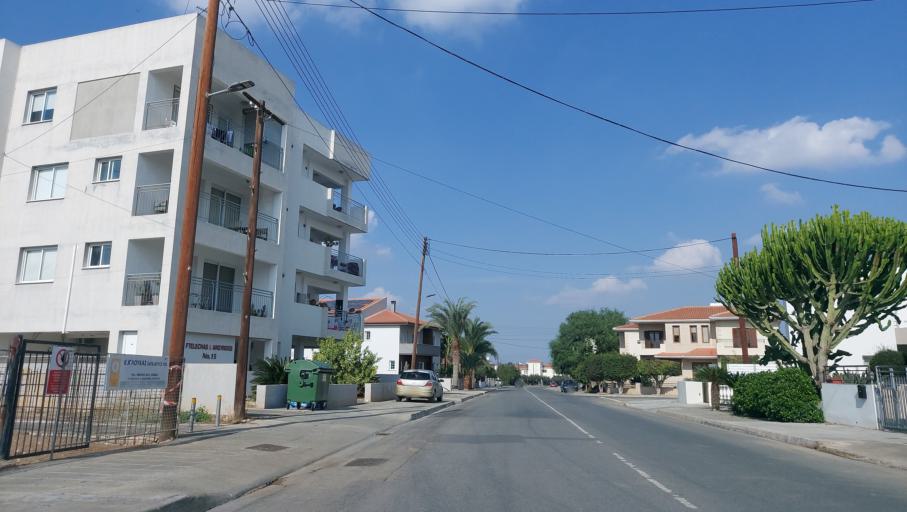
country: CY
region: Lefkosia
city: Tseri
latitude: 35.1030
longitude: 33.3073
